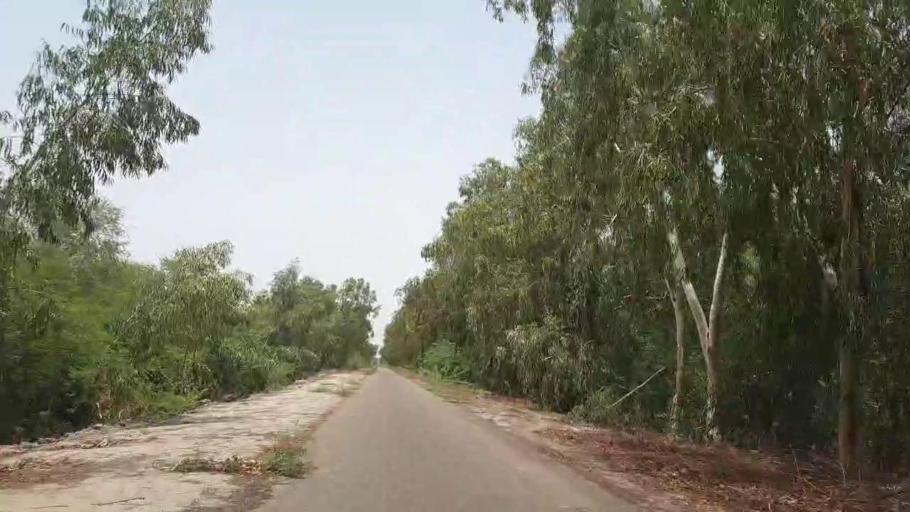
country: PK
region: Sindh
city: Sakrand
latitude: 26.0961
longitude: 68.2376
